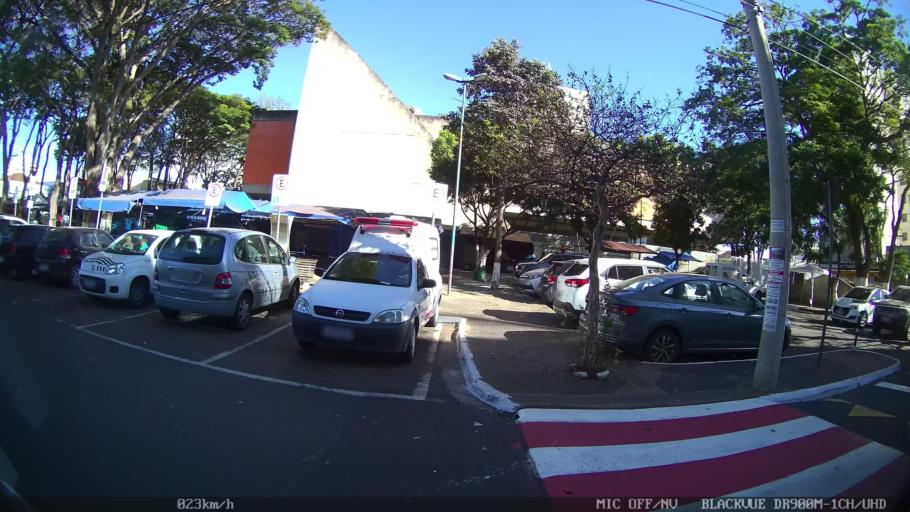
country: BR
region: Sao Paulo
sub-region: Franca
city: Franca
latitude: -20.5379
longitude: -47.3990
